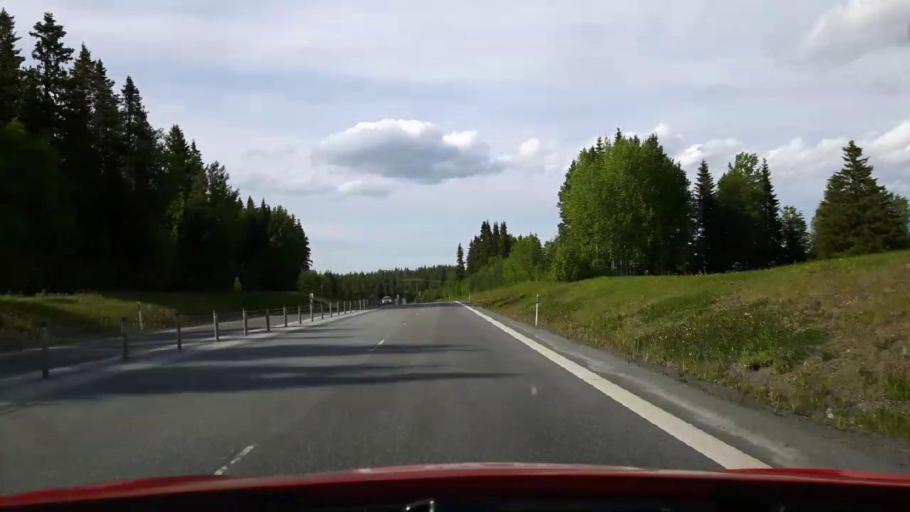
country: SE
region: Jaemtland
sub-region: OEstersunds Kommun
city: Brunflo
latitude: 63.1328
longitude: 14.7901
